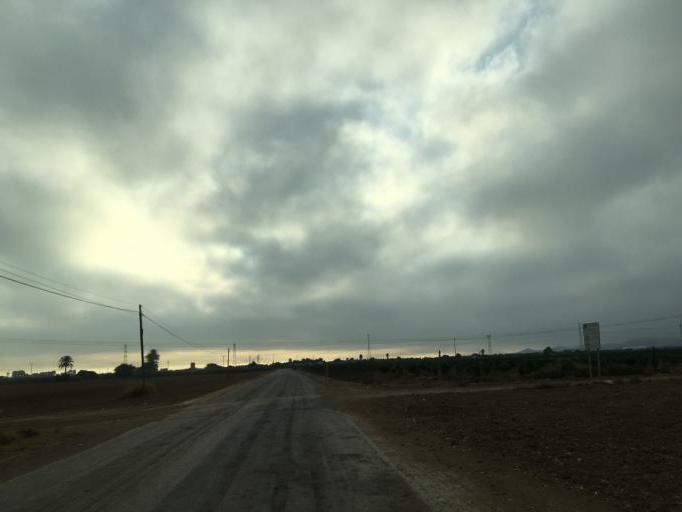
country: ES
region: Murcia
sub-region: Murcia
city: Cartagena
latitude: 37.6624
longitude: -0.9436
